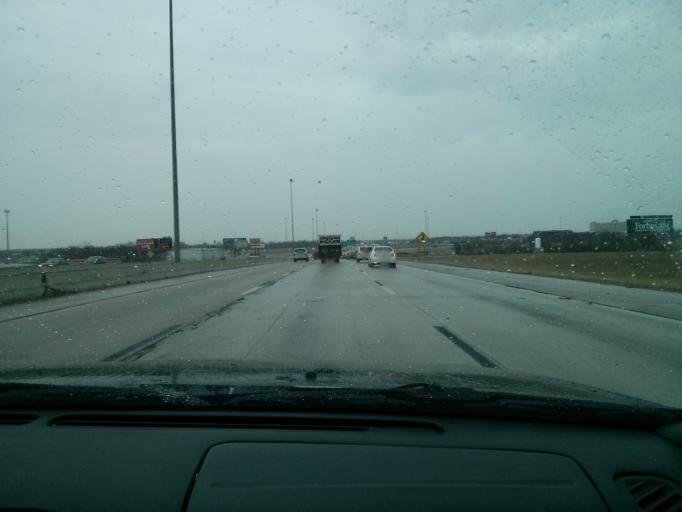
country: US
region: Oklahoma
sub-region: Tulsa County
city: Broken Arrow
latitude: 36.0908
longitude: -95.8589
